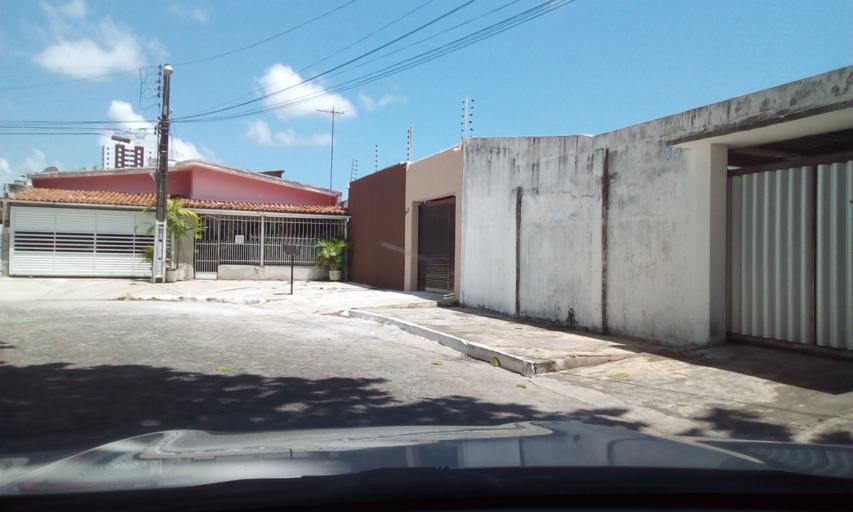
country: BR
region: Paraiba
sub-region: Joao Pessoa
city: Joao Pessoa
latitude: -7.1123
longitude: -34.8632
